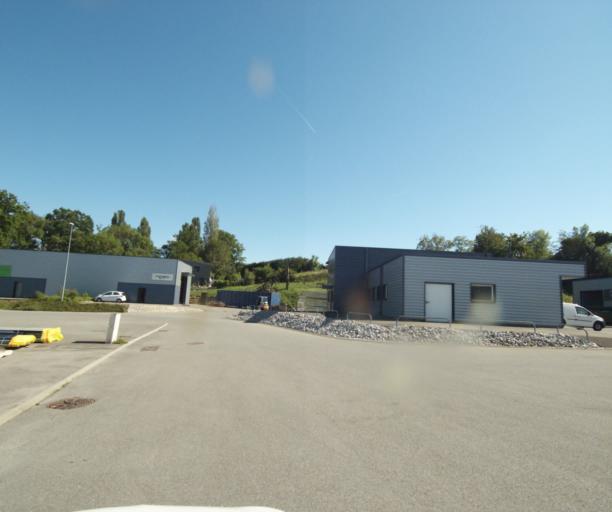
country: FR
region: Rhone-Alpes
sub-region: Departement de la Haute-Savoie
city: Sciez
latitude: 46.3291
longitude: 6.3800
